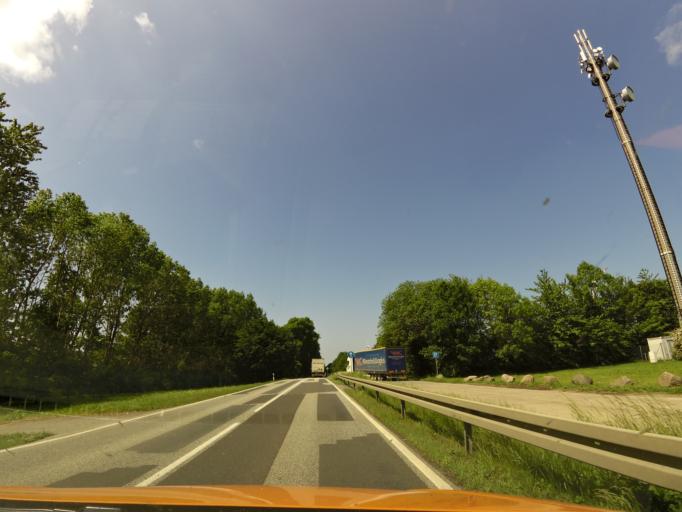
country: DE
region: Mecklenburg-Vorpommern
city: Selmsdorf
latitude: 53.8674
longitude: 10.9004
